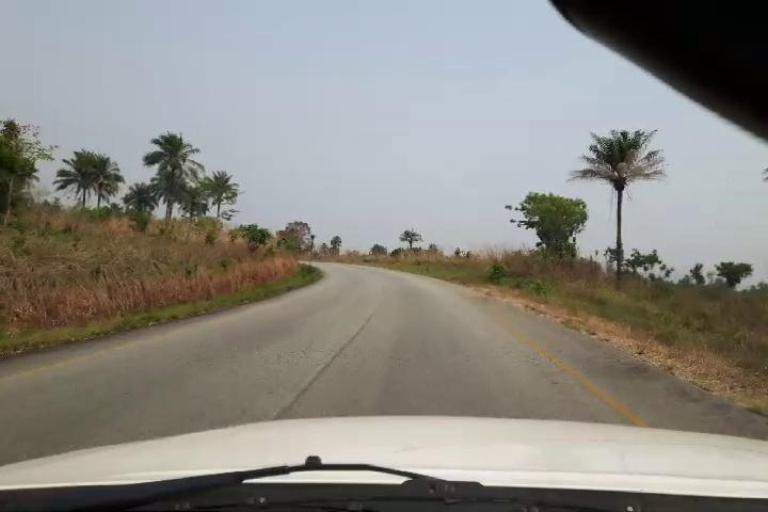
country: SL
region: Southern Province
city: Largo
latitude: 8.3032
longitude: -12.2011
